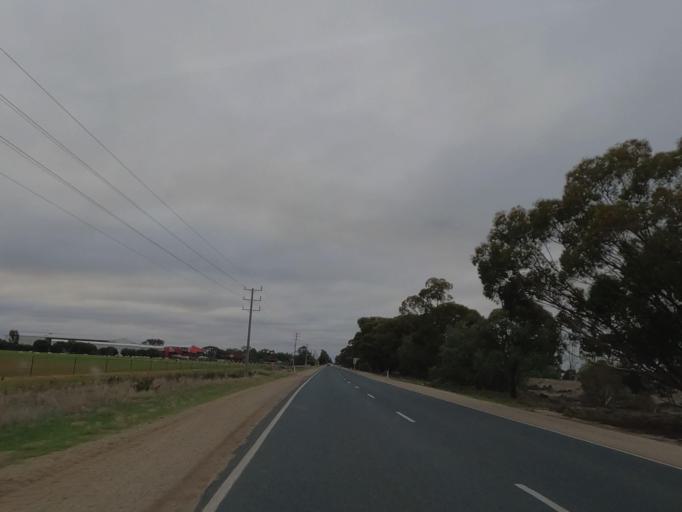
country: AU
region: Victoria
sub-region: Swan Hill
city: Swan Hill
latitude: -35.3905
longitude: 143.5699
